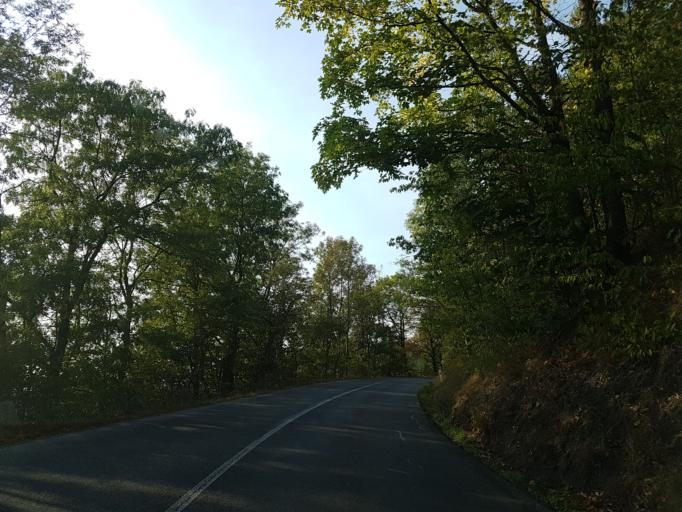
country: CZ
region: Liberecky
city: Mala Skala
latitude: 50.6523
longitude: 15.1607
